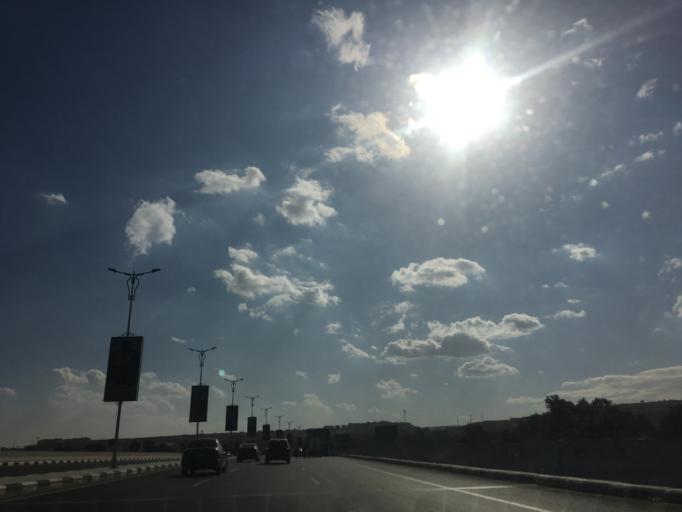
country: EG
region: Muhafazat al Qahirah
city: Cairo
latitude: 30.0433
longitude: 31.3079
